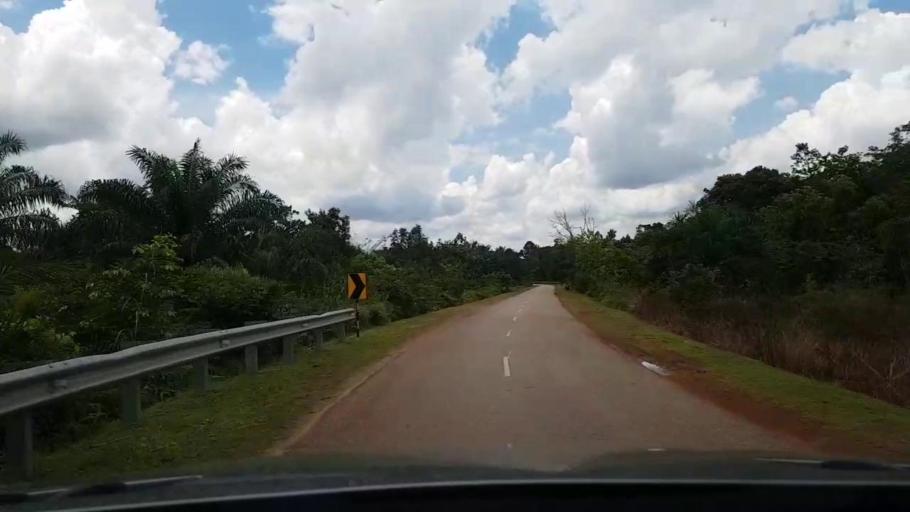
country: MY
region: Pahang
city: Pekan
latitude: 3.1135
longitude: 102.9766
